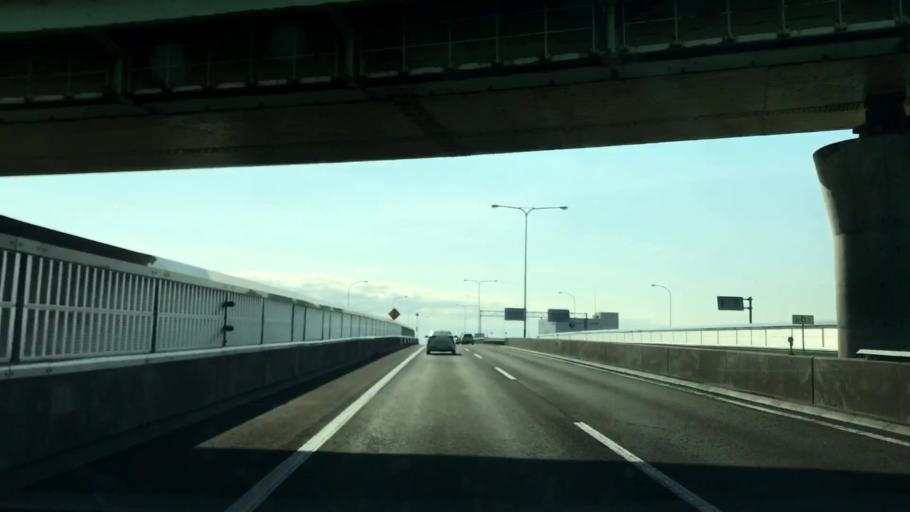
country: JP
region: Hokkaido
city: Sapporo
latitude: 43.0760
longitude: 141.4209
